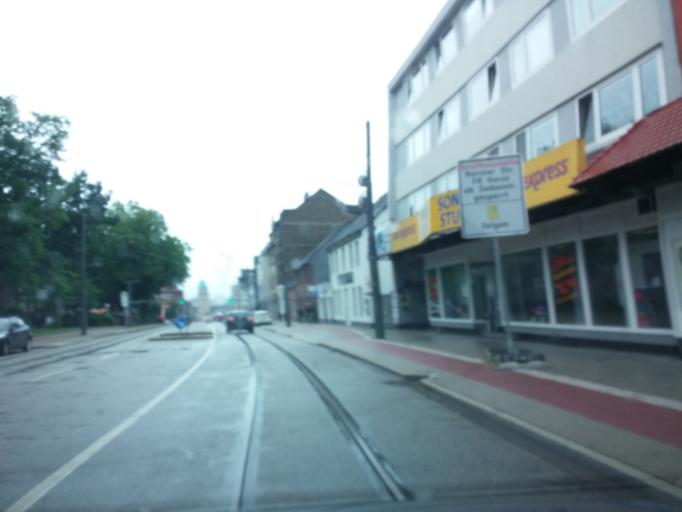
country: DE
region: North Rhine-Westphalia
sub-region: Regierungsbezirk Munster
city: Gladbeck
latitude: 51.5754
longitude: 7.0487
